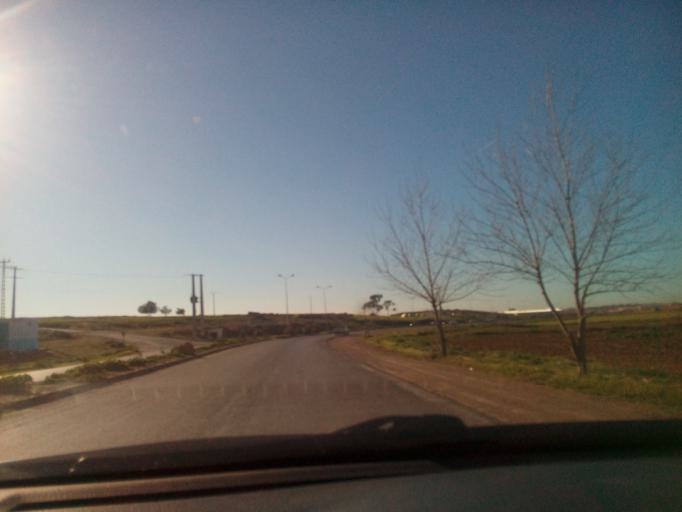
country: DZ
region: Relizane
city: Relizane
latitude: 35.7116
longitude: 0.5537
